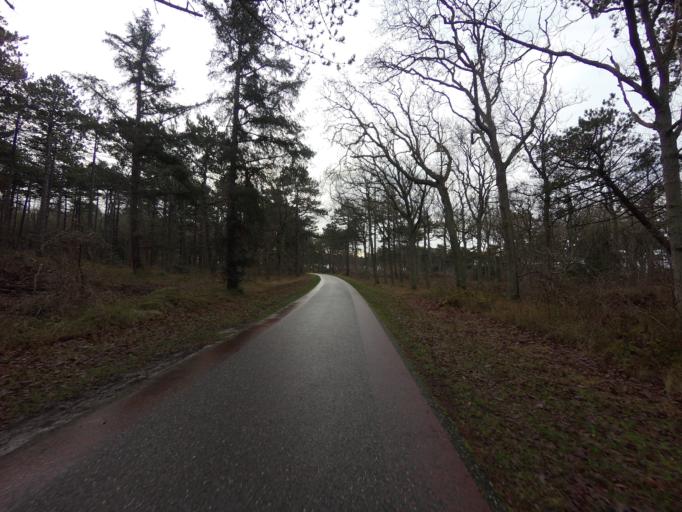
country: NL
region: North Holland
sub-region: Gemeente Texel
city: Den Burg
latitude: 53.0462
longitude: 4.7262
